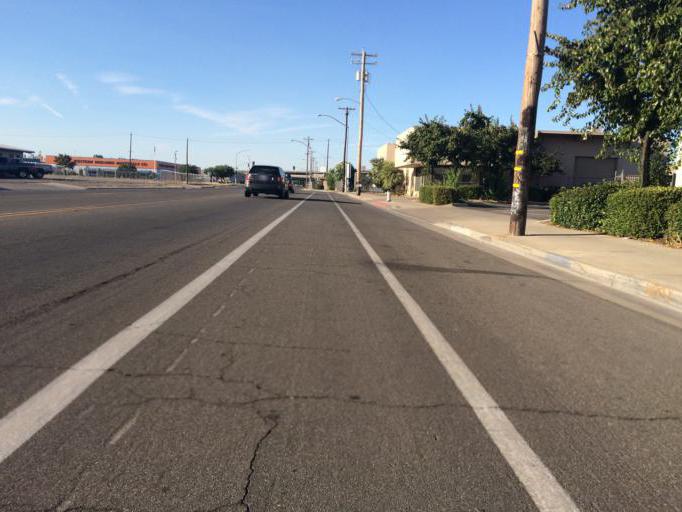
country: US
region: California
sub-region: Fresno County
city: Fresno
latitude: 36.7594
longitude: -119.7456
